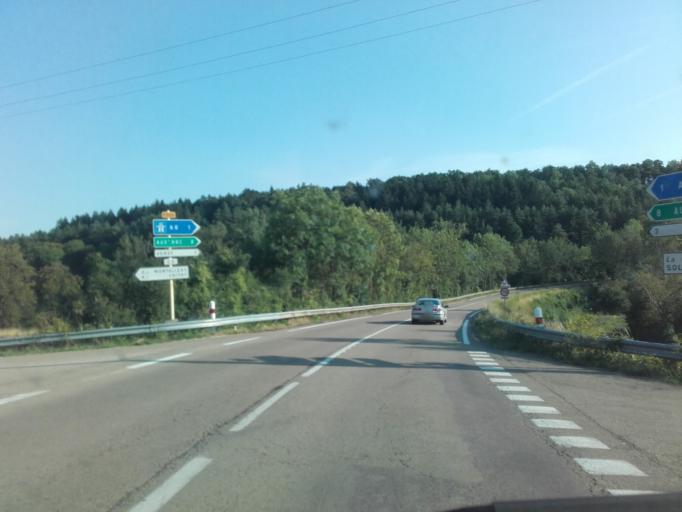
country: FR
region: Bourgogne
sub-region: Departement de l'Yonne
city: Venoy
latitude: 47.8033
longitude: 3.6675
